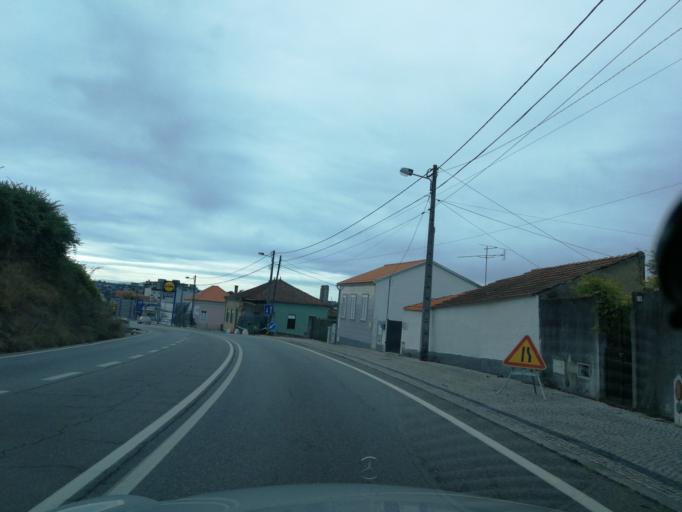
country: PT
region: Aveiro
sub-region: Agueda
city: Agueda
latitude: 40.5794
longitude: -8.4510
